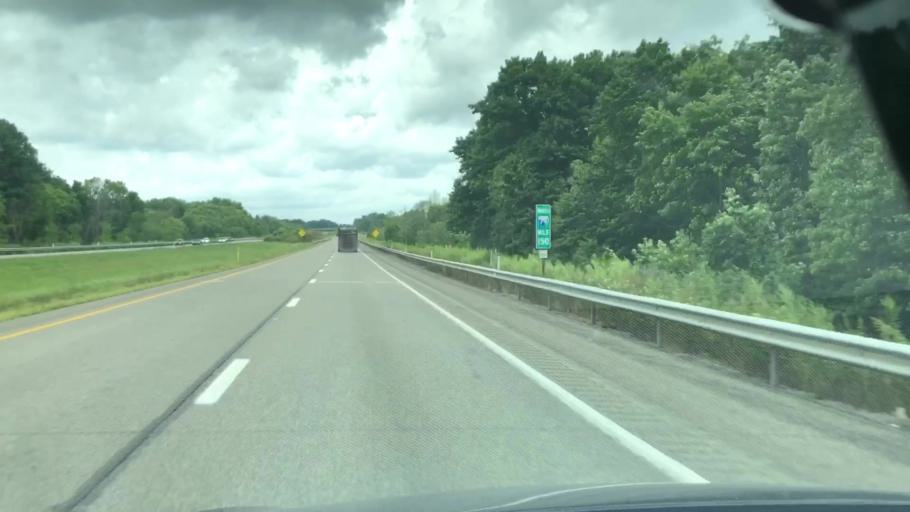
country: US
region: Pennsylvania
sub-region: Crawford County
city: Meadville
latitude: 41.6593
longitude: -80.2062
